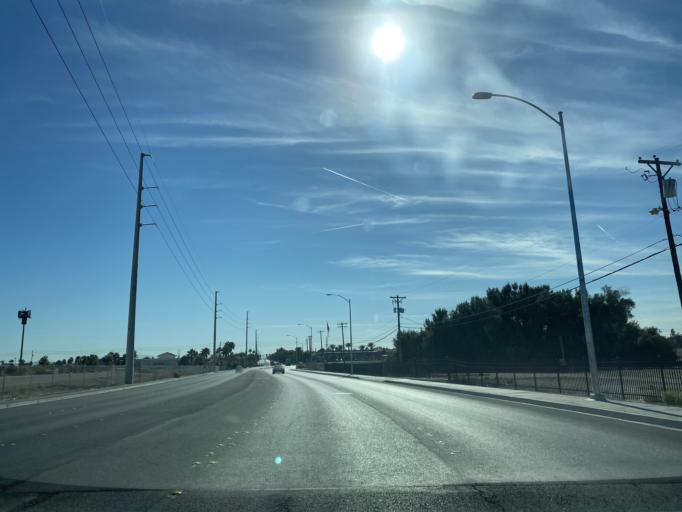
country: US
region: Nevada
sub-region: Clark County
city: North Las Vegas
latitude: 36.2425
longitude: -115.1437
